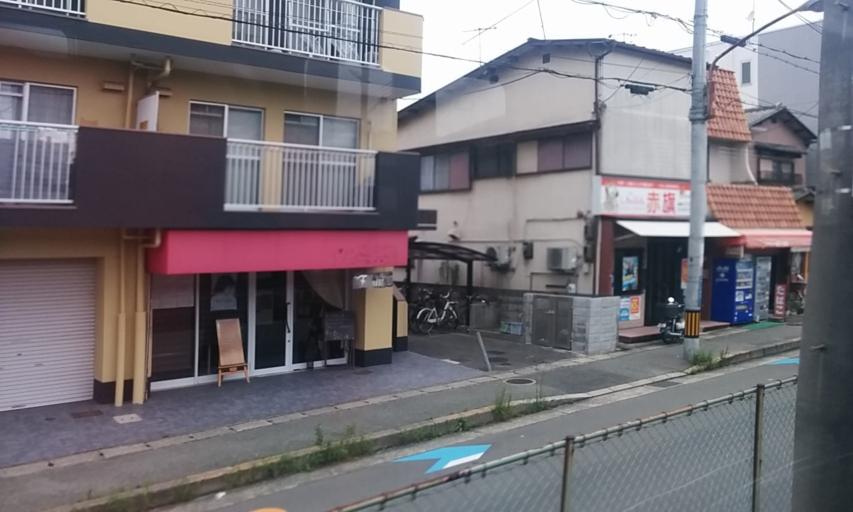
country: JP
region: Osaka
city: Mino
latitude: 34.8260
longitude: 135.4663
